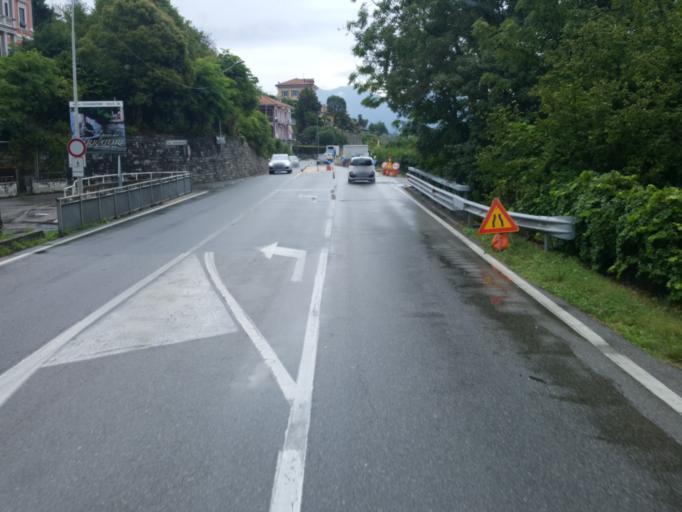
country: IT
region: Piedmont
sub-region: Provincia Verbano-Cusio-Ossola
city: Verbania
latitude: 45.9328
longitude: 8.5370
